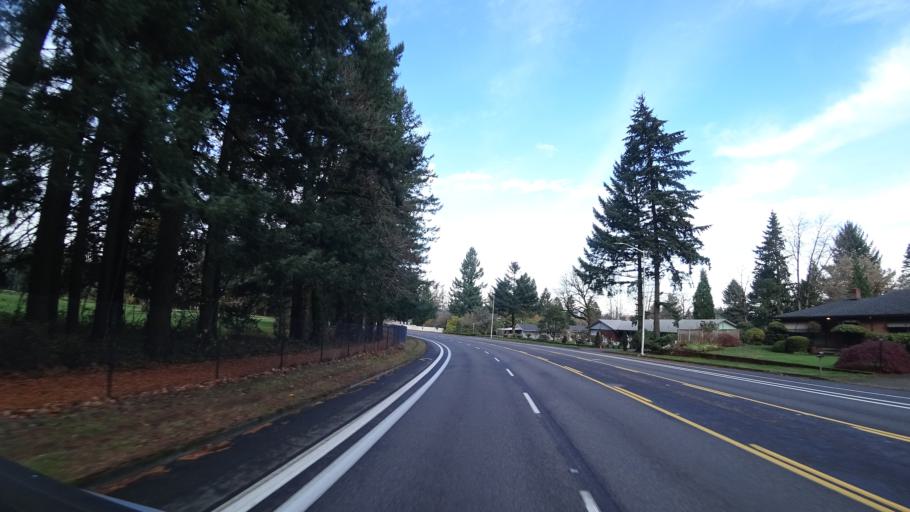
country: US
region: Oregon
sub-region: Multnomah County
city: Fairview
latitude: 45.5292
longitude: -122.5089
